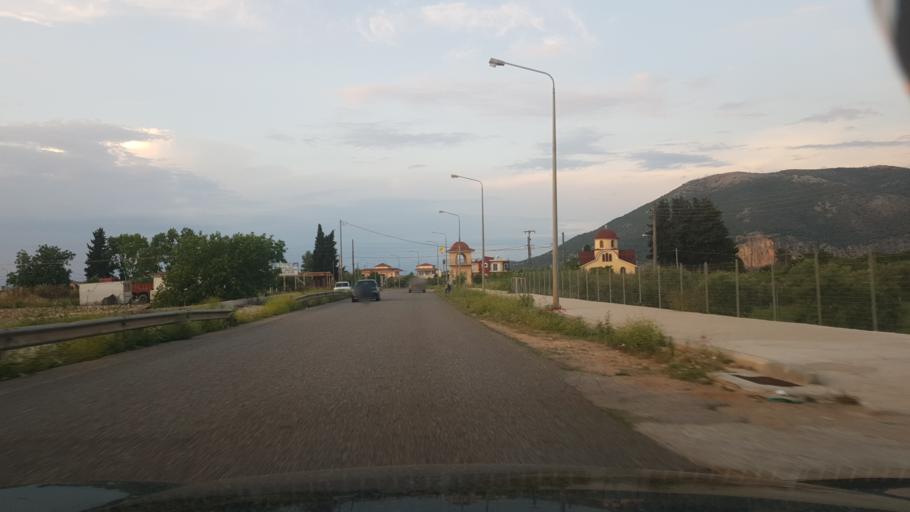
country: GR
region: West Greece
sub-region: Nomos Aitolias kai Akarnanias
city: Vonitsa
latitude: 38.9087
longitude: 20.8855
